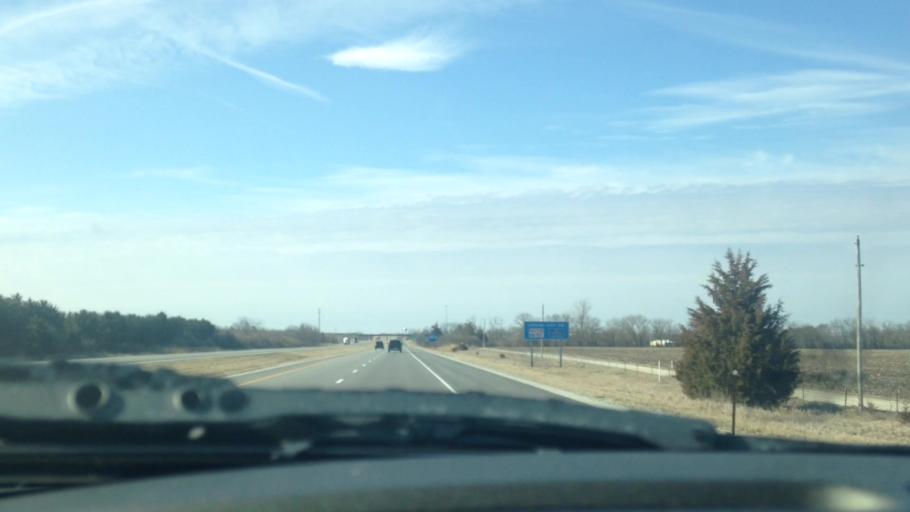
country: US
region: Illinois
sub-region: Ford County
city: Paxton
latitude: 40.4836
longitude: -88.0988
